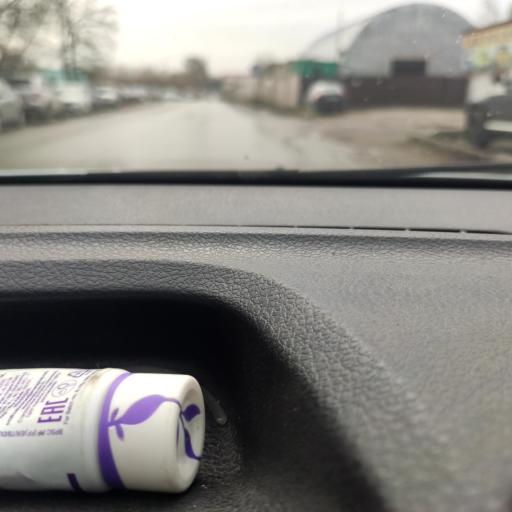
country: RU
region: Bashkortostan
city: Ufa
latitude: 54.8075
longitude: 56.0700
